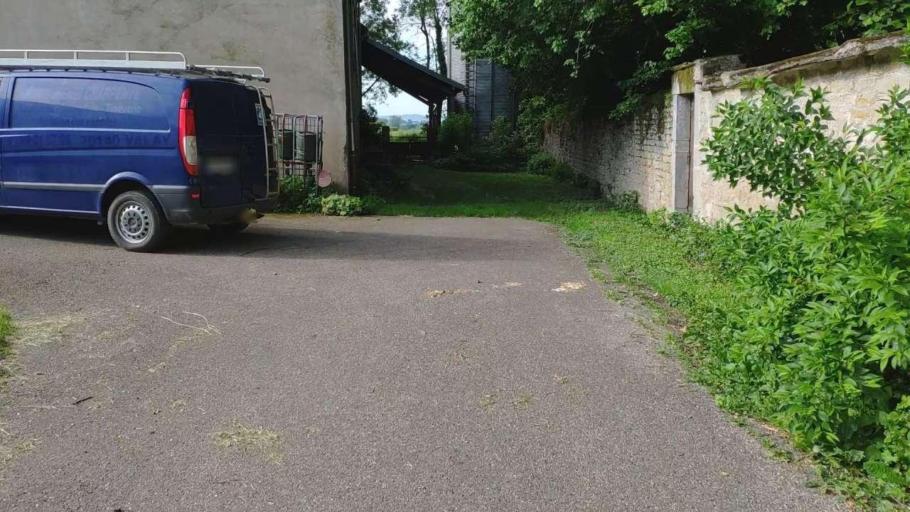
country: FR
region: Franche-Comte
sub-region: Departement du Jura
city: Bletterans
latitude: 46.7353
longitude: 5.4656
